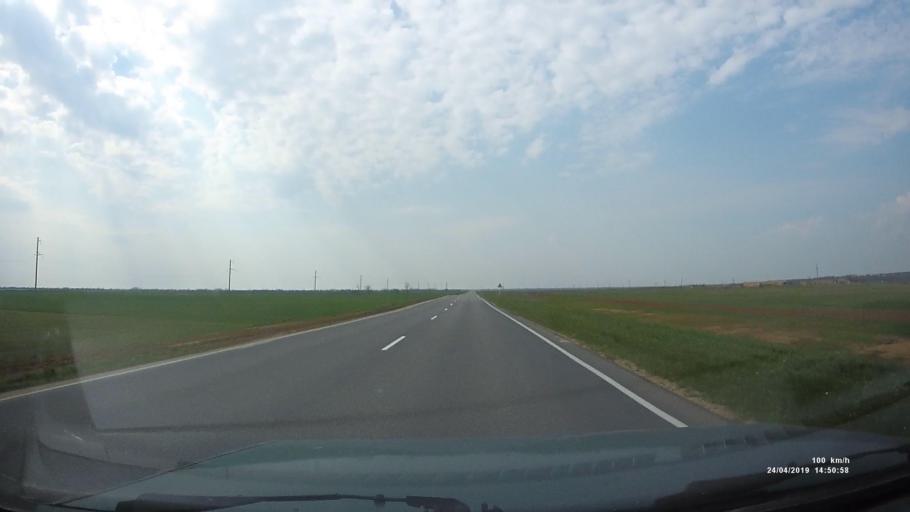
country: RU
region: Rostov
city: Remontnoye
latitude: 46.5213
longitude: 43.7095
